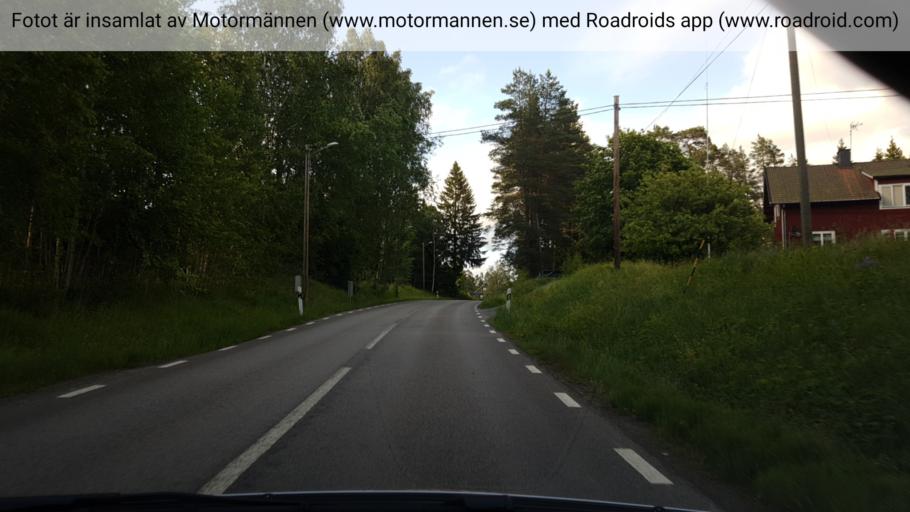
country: SE
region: OErebro
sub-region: Karlskoga Kommun
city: Karlskoga
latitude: 59.4004
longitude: 14.6388
